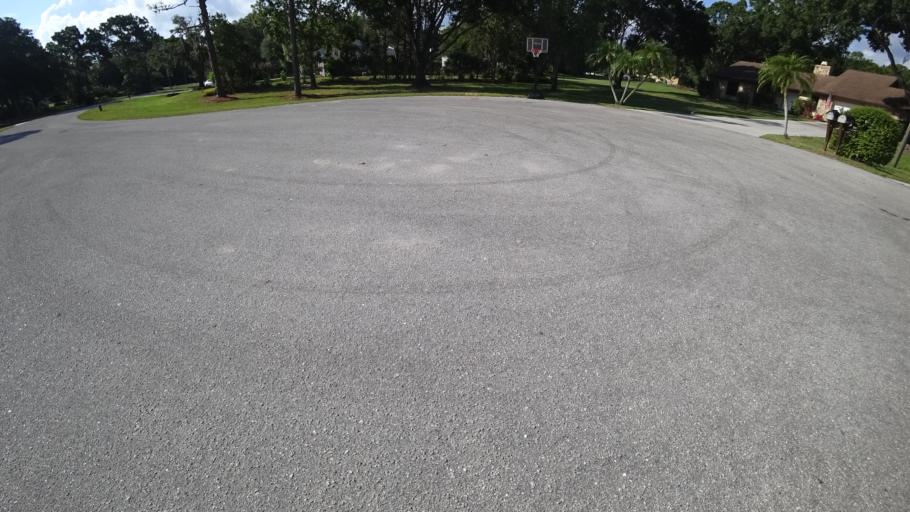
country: US
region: Florida
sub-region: Sarasota County
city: Desoto Lakes
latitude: 27.4279
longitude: -82.4528
